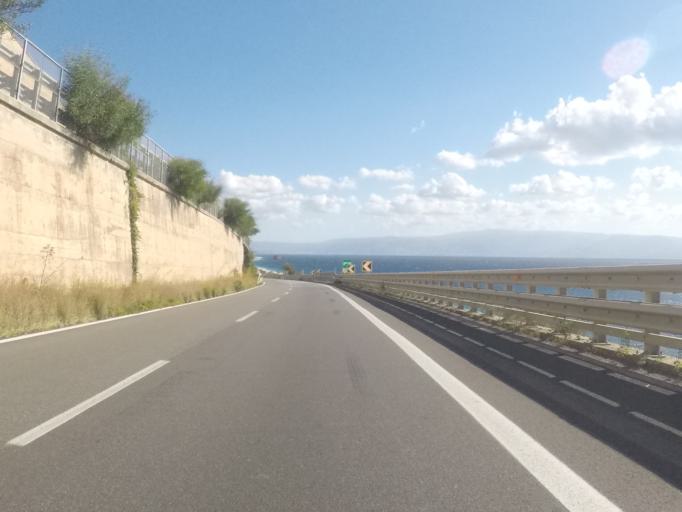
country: IT
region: Sicily
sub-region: Messina
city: Itala
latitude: 38.0301
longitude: 15.4449
